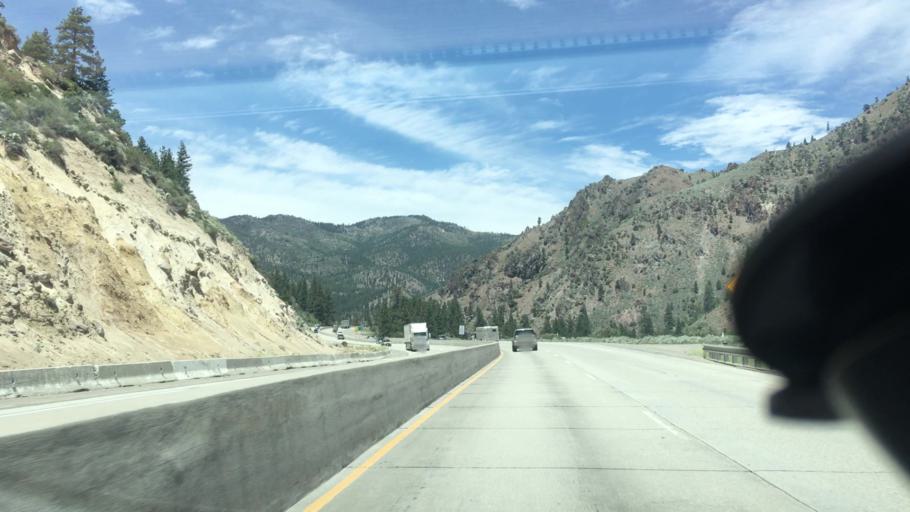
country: US
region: Nevada
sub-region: Washoe County
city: Verdi
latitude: 39.4089
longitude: -120.0271
